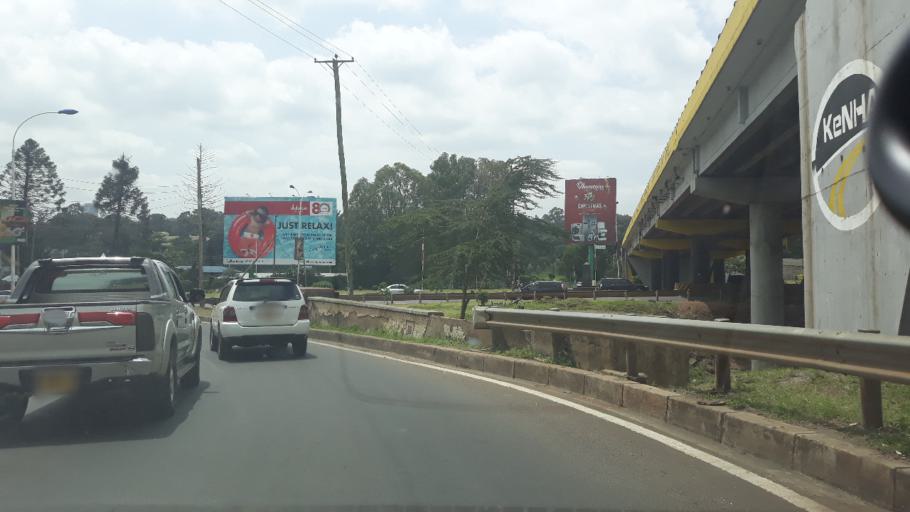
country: KE
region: Nairobi Area
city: Nairobi
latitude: -1.2743
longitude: 36.8127
